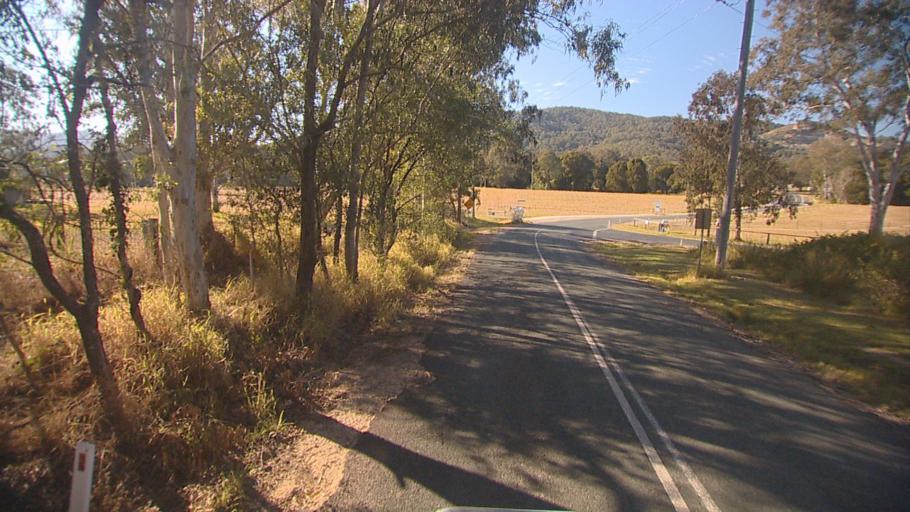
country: AU
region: Queensland
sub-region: Gold Coast
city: Ormeau Hills
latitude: -27.8243
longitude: 153.1766
